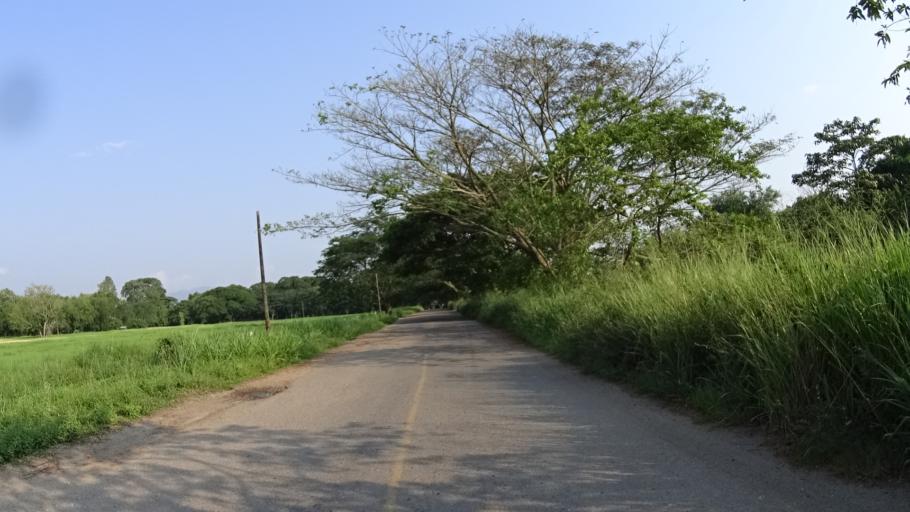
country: CO
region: Cundinamarca
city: Puerto Salgar
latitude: 5.5041
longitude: -74.6887
